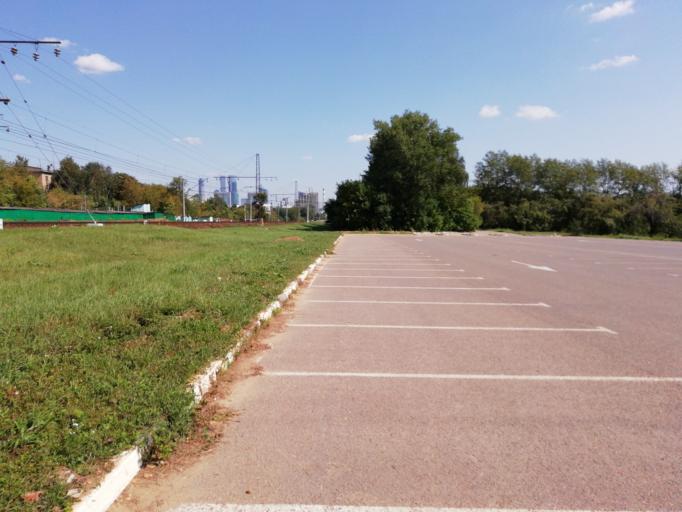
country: RU
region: Moscow
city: Davydkovo
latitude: 55.7308
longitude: 37.4767
